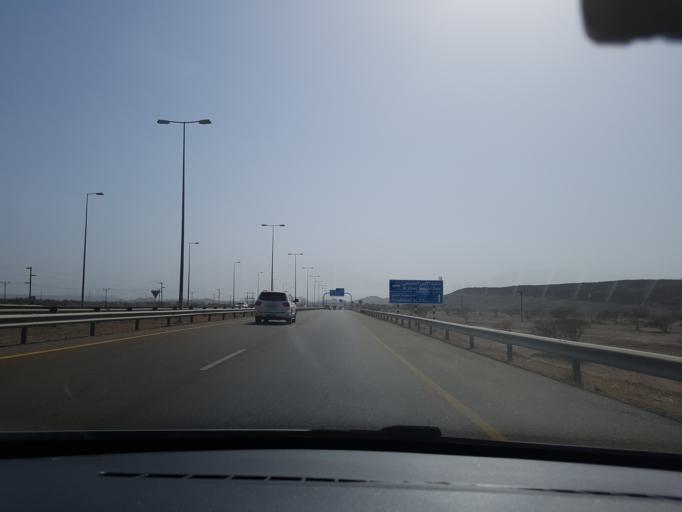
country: OM
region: Al Batinah
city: Al Liwa'
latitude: 24.3950
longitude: 56.5713
